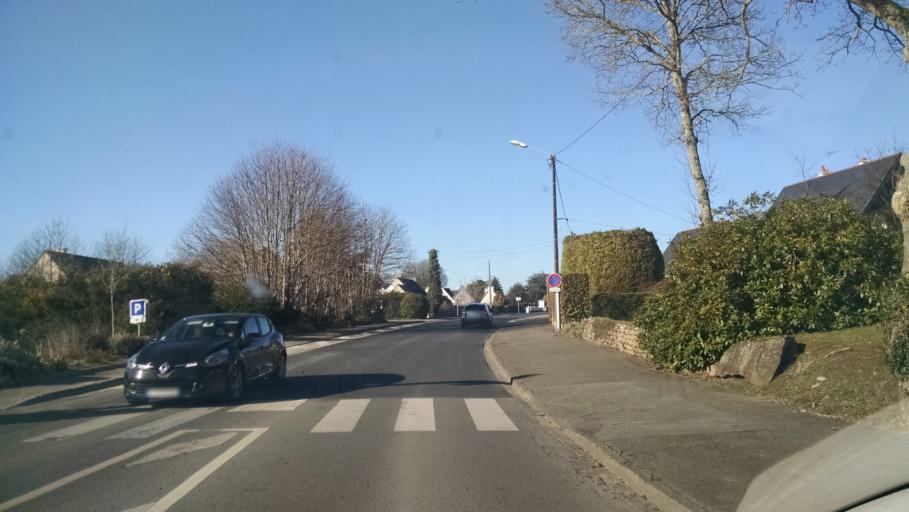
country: FR
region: Brittany
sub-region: Departement du Morbihan
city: Guidel-Plage
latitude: 47.7928
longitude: -3.4939
